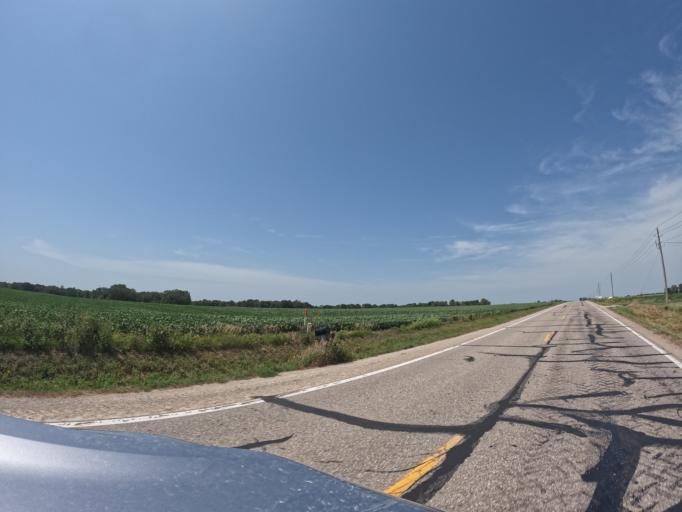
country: US
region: Iowa
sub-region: Henry County
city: Mount Pleasant
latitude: 40.9904
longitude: -91.6123
